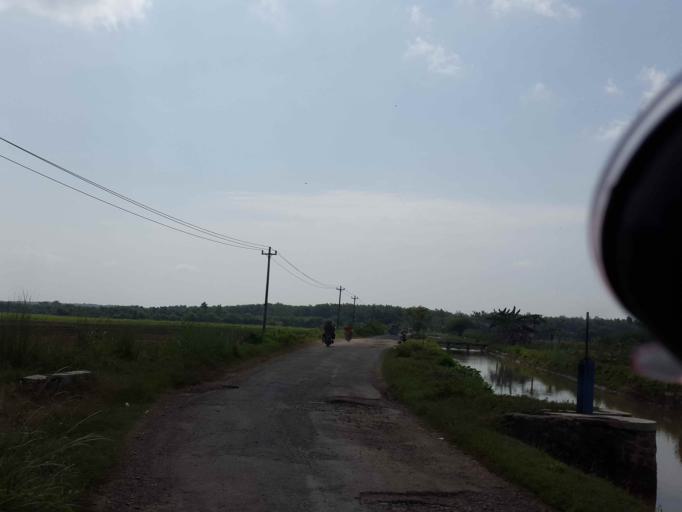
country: ID
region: Central Java
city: Pemalang
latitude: -6.9507
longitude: 109.3569
